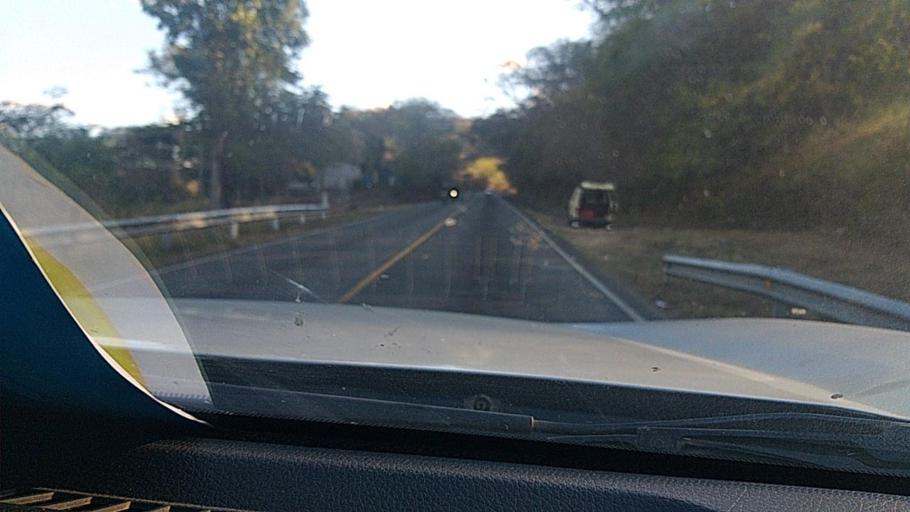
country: NI
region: Esteli
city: Condega
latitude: 13.2634
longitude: -86.3540
